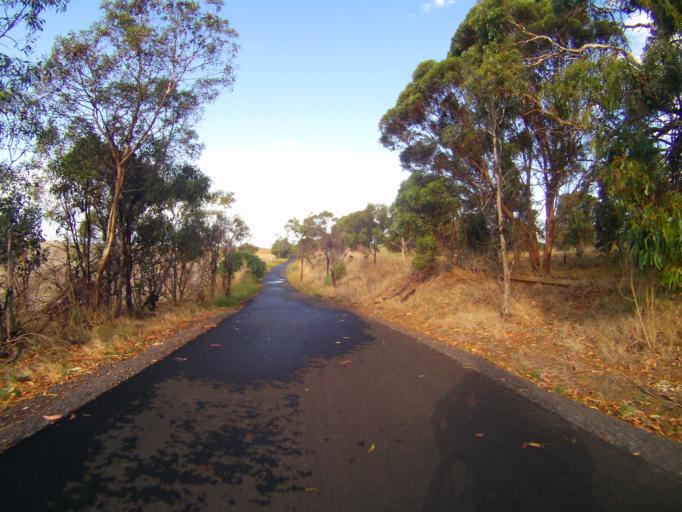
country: AU
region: Victoria
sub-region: Greater Geelong
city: Clifton Springs
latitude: -38.1797
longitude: 144.5311
